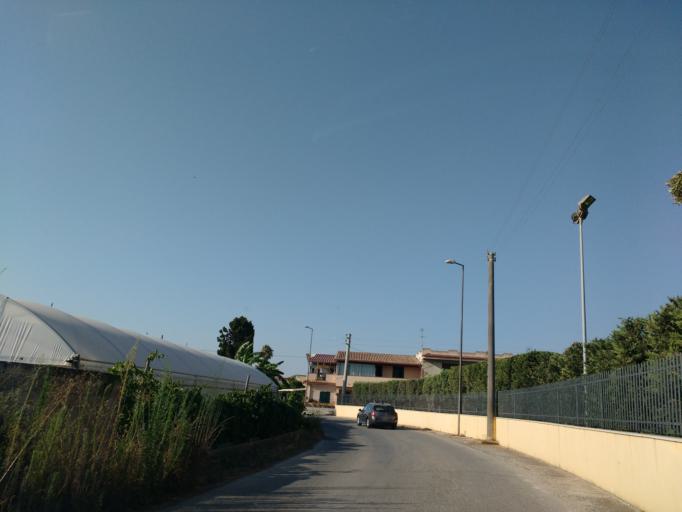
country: IT
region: Sicily
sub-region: Ragusa
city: Cava d'Aliga
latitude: 36.7472
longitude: 14.6712
